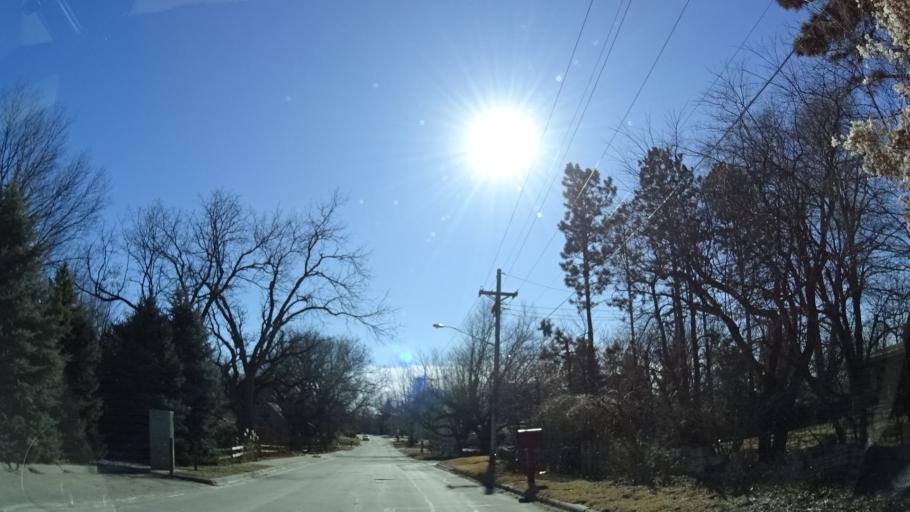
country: US
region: Nebraska
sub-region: Sarpy County
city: Bellevue
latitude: 41.1514
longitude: -95.9002
